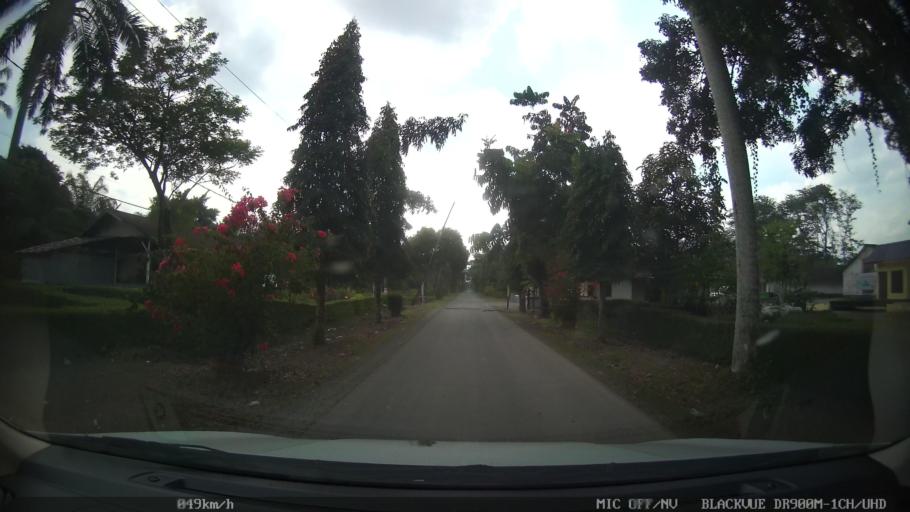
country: ID
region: North Sumatra
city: Binjai
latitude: 3.6354
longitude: 98.5160
